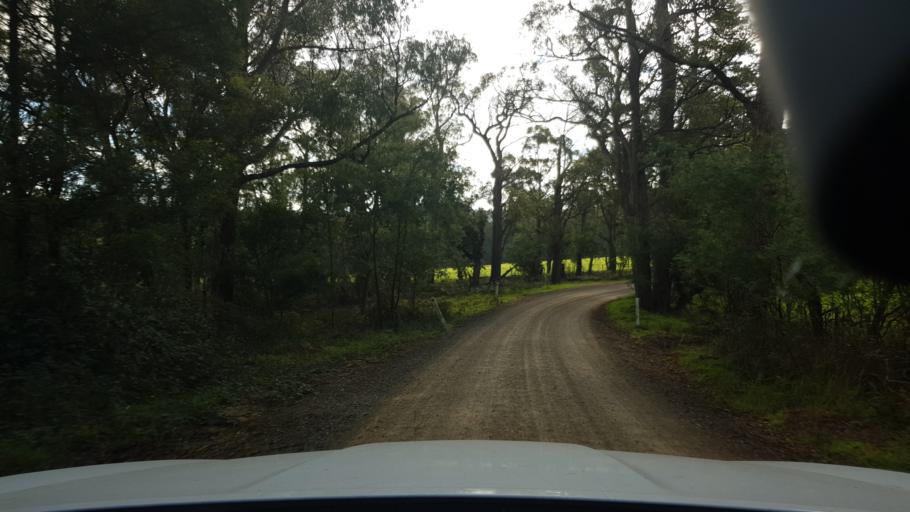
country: AU
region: Victoria
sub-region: East Gippsland
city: Bairnsdale
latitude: -37.7738
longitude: 147.5678
